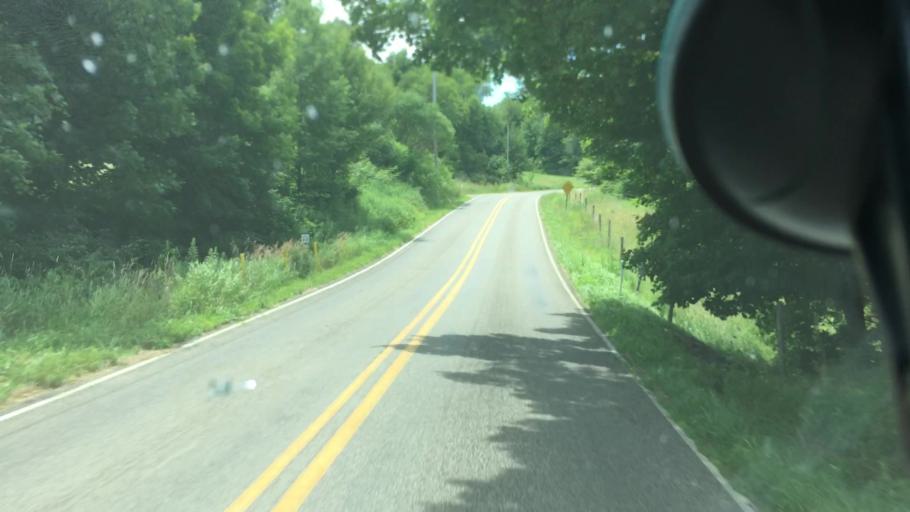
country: US
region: Pennsylvania
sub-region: Mercer County
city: Mercer
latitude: 41.2260
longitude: -80.2031
